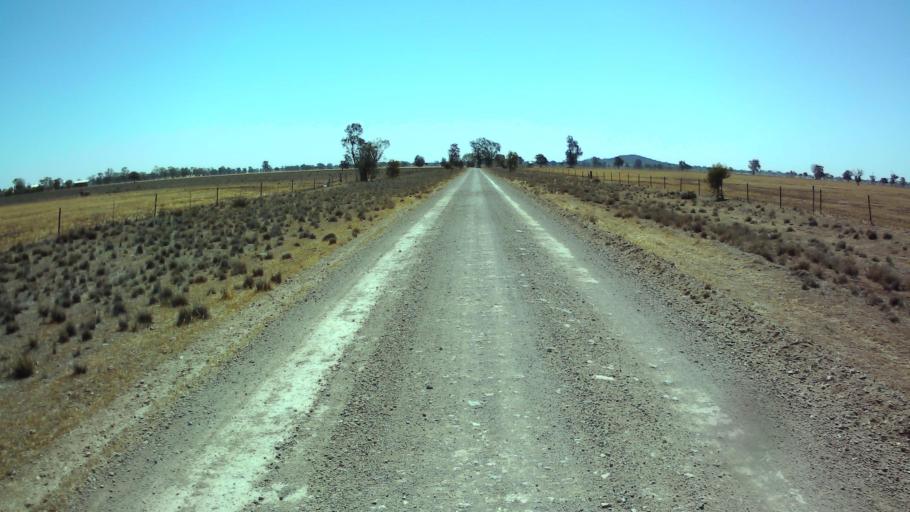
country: AU
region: New South Wales
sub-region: Forbes
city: Forbes
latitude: -33.7464
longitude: 147.7190
